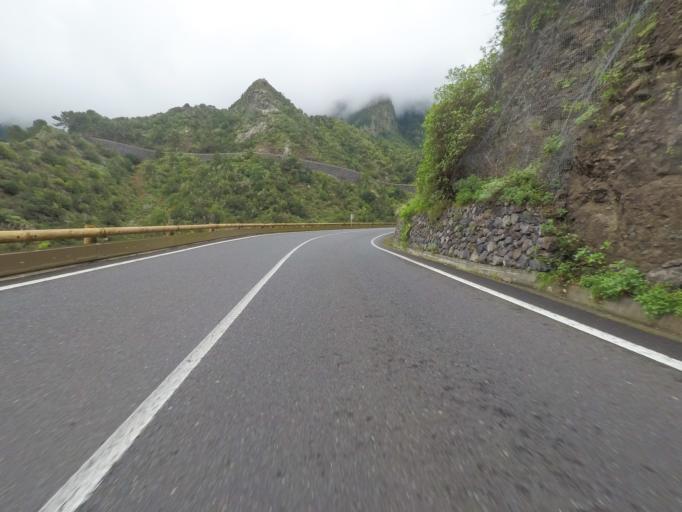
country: ES
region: Canary Islands
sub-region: Provincia de Santa Cruz de Tenerife
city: Hermigua
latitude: 28.1376
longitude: -17.2011
